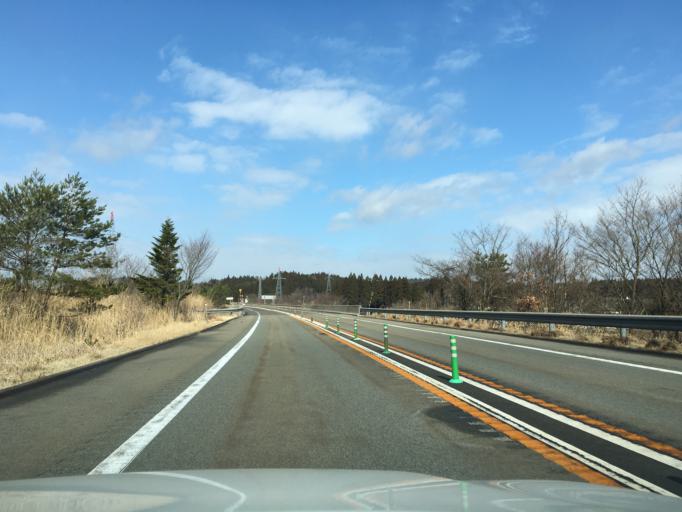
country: JP
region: Akita
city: Akita
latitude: 39.7369
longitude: 140.1737
